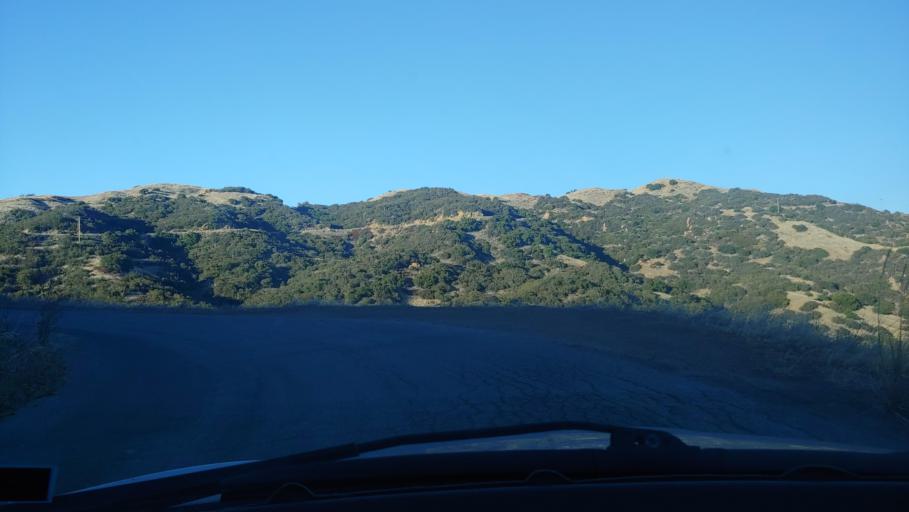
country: US
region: California
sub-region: Santa Barbara County
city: Goleta
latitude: 34.5150
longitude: -119.7922
